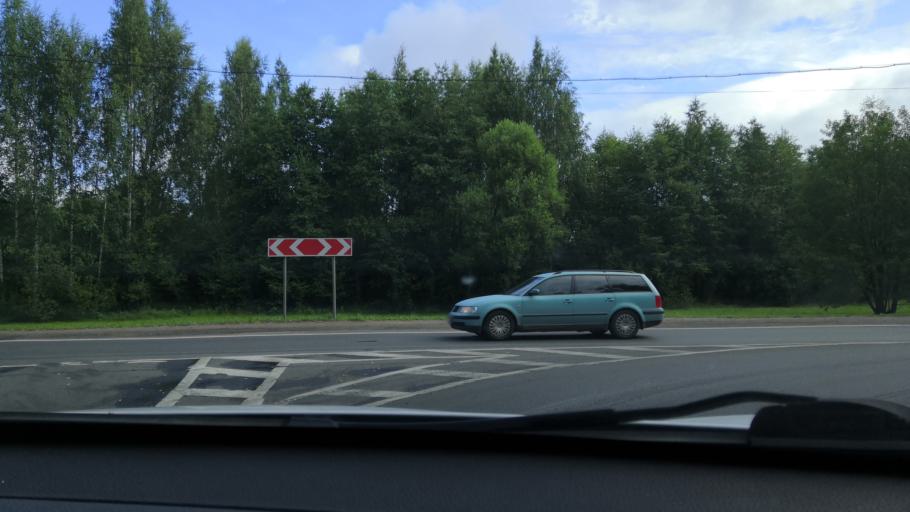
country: RU
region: St.-Petersburg
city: Pavlovsk
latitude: 59.6970
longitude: 30.4347
